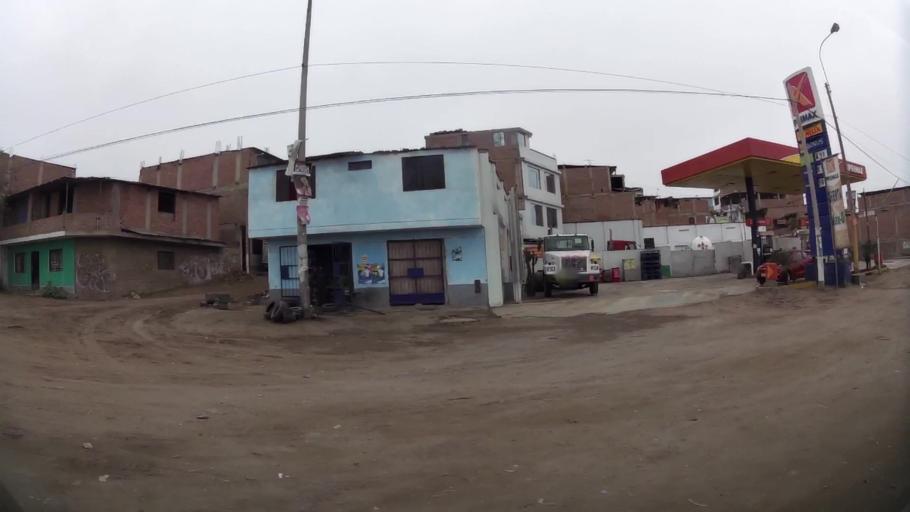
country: PE
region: Lima
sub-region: Lima
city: Surco
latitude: -12.2249
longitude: -76.9191
